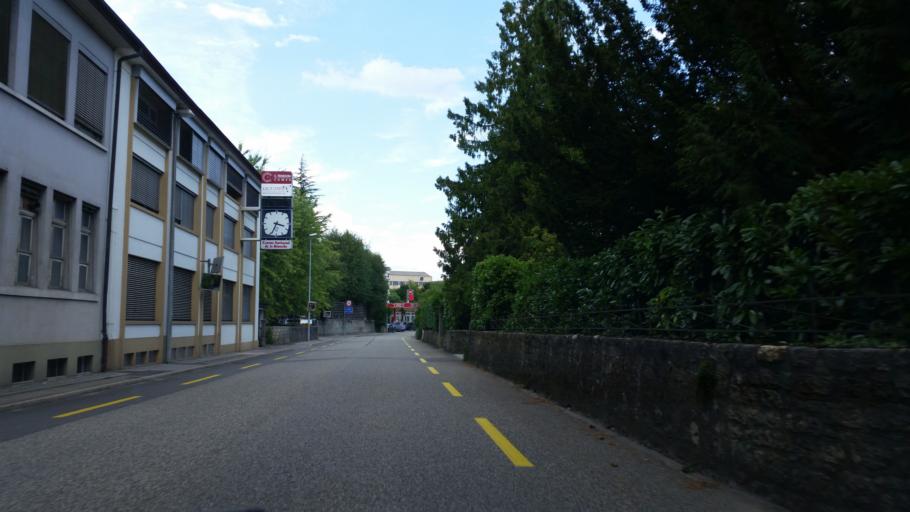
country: CH
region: Neuchatel
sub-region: Boudry District
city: Gorgier
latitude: 46.8968
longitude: 6.7799
